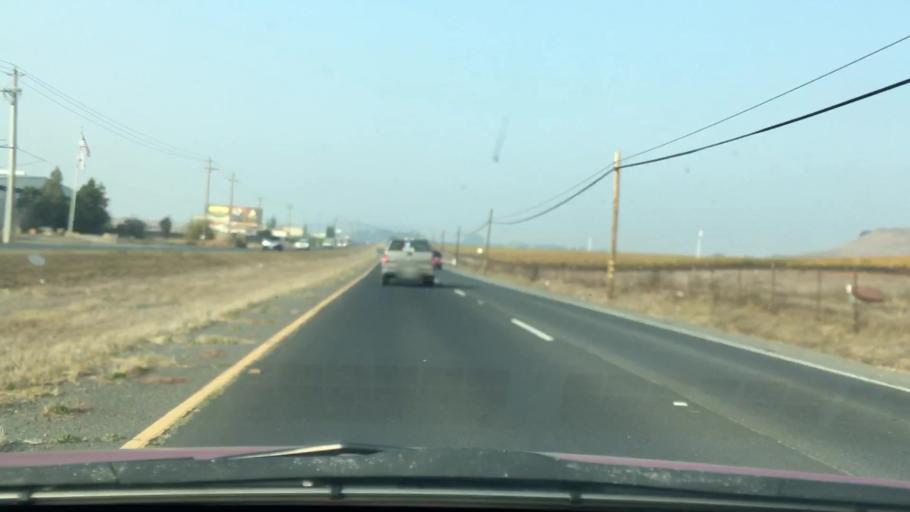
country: US
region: California
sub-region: Napa County
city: American Canyon
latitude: 38.1996
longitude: -122.2561
